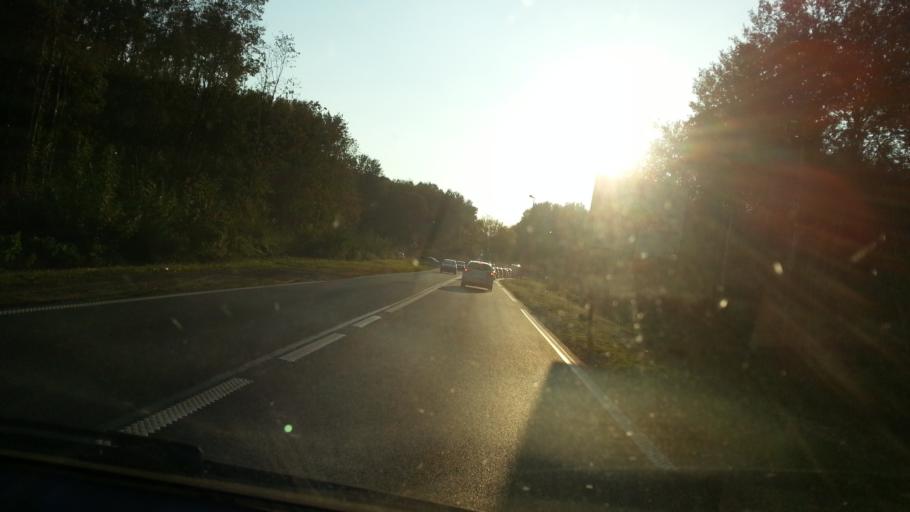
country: FR
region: Picardie
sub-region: Departement de l'Oise
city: Brenouille
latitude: 49.3141
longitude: 2.5561
